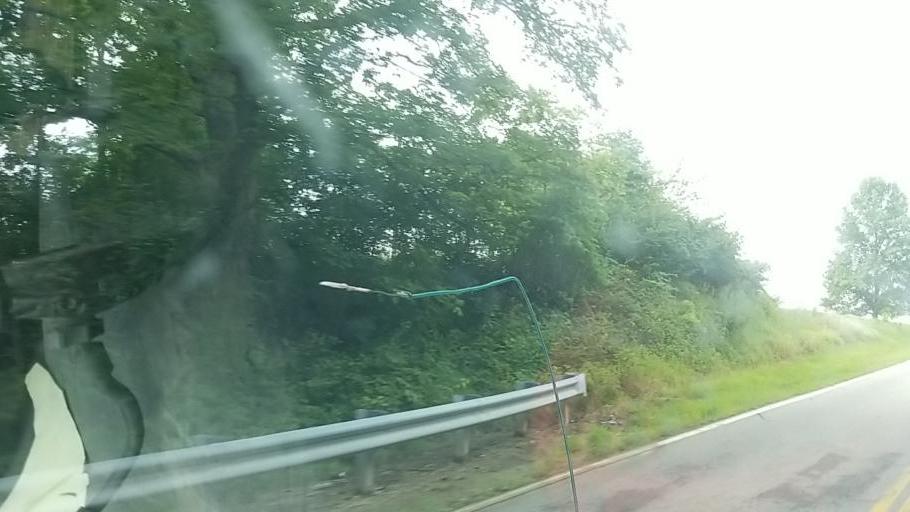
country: US
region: Ohio
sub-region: Madison County
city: Mount Sterling
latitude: 39.7525
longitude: -83.1681
